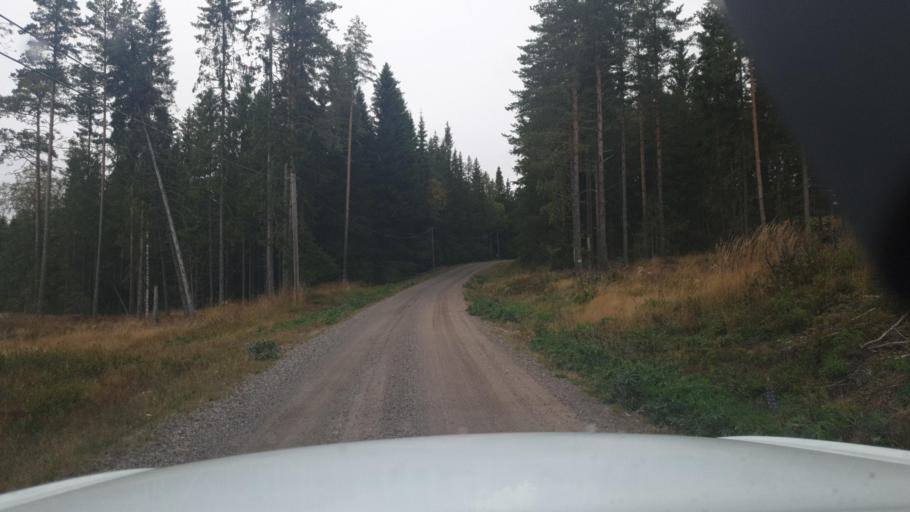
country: SE
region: Vaermland
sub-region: Eda Kommun
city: Charlottenberg
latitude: 60.1477
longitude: 12.5956
